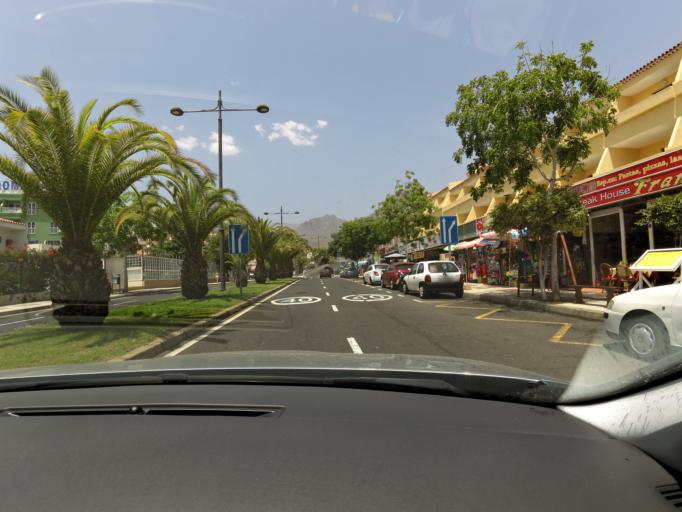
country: ES
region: Canary Islands
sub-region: Provincia de Santa Cruz de Tenerife
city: Playa de las Americas
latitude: 28.0801
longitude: -16.7307
